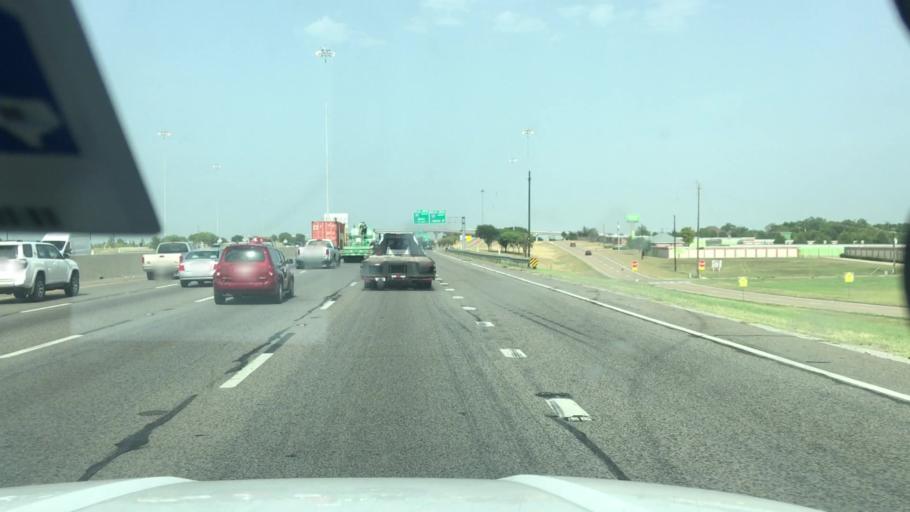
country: US
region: Texas
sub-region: Dallas County
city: DeSoto
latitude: 32.6420
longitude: -96.8312
